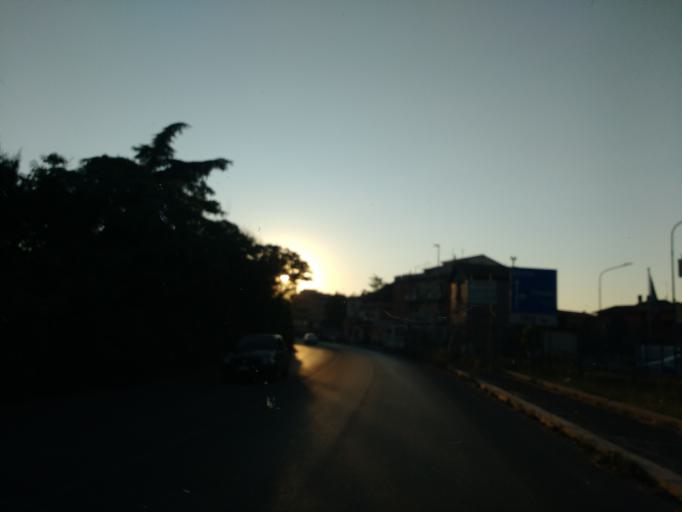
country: IT
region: Latium
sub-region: Citta metropolitana di Roma Capitale
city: Bagni di Tivoli
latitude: 41.9537
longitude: 12.7125
